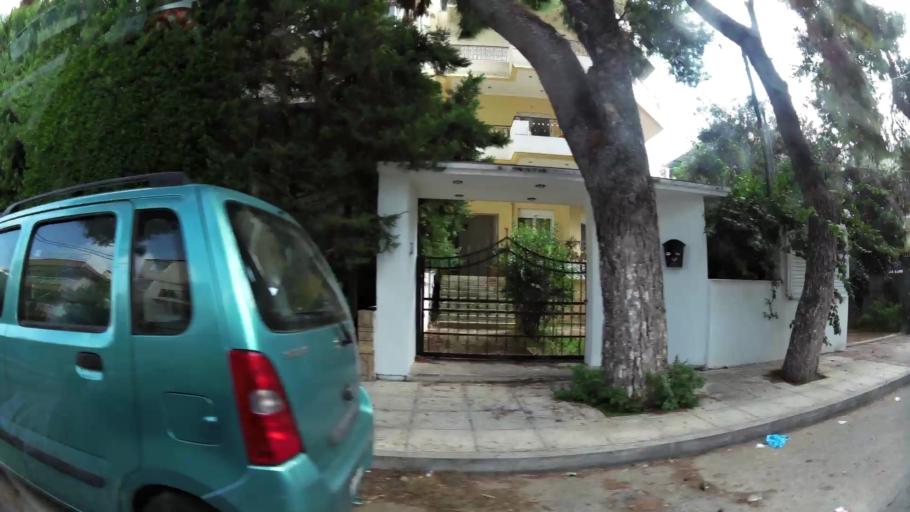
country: GR
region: Attica
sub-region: Nomarchia Athinas
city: Cholargos
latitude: 37.9958
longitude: 23.8069
